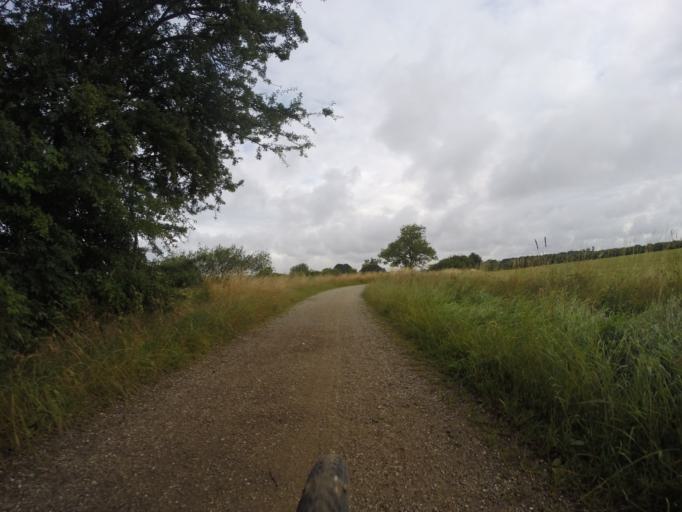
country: DK
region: Capital Region
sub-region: Hoje-Taastrup Kommune
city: Taastrup
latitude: 55.6937
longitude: 12.3167
